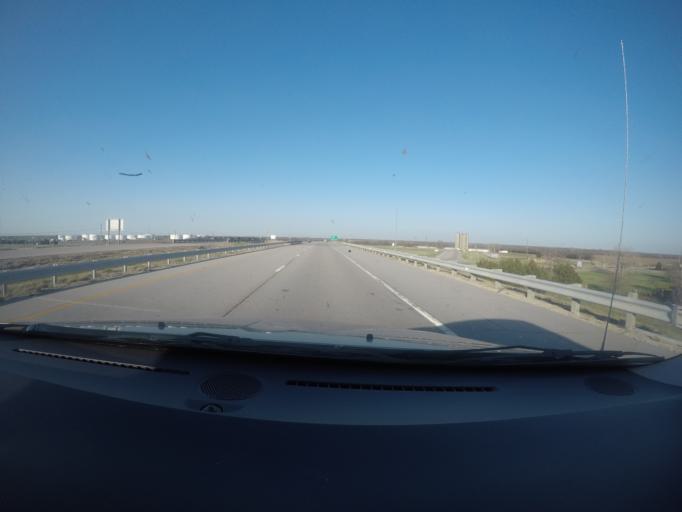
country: US
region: Kansas
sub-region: McPherson County
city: McPherson
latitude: 38.3345
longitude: -97.6691
